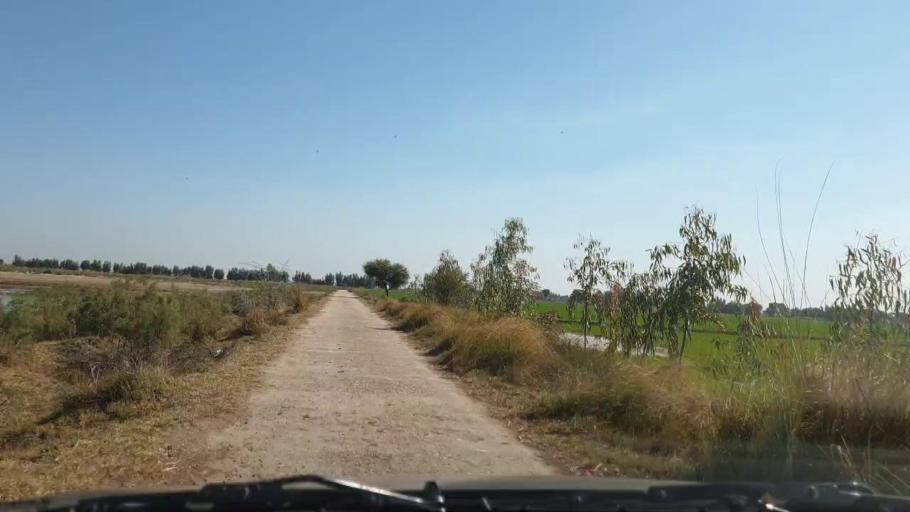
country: PK
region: Sindh
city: Sinjhoro
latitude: 26.1336
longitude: 68.8433
